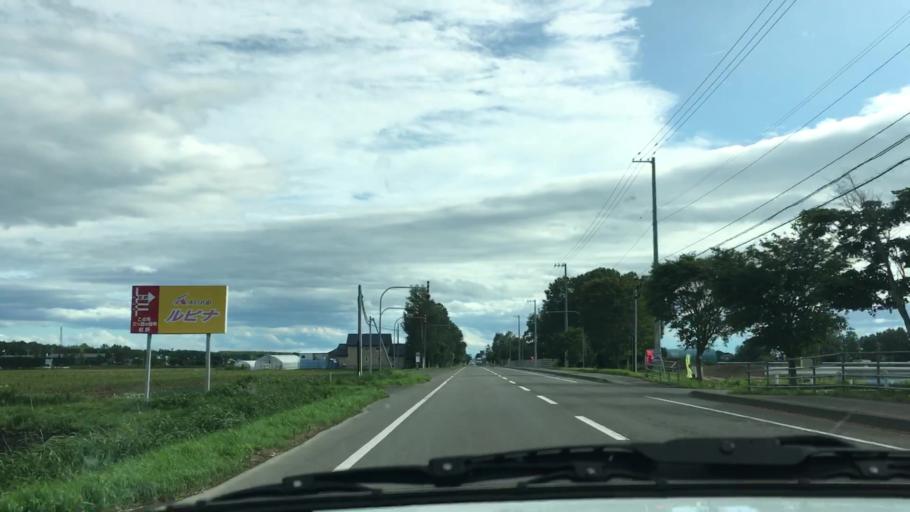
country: JP
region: Hokkaido
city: Otofuke
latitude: 43.2450
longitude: 143.2978
